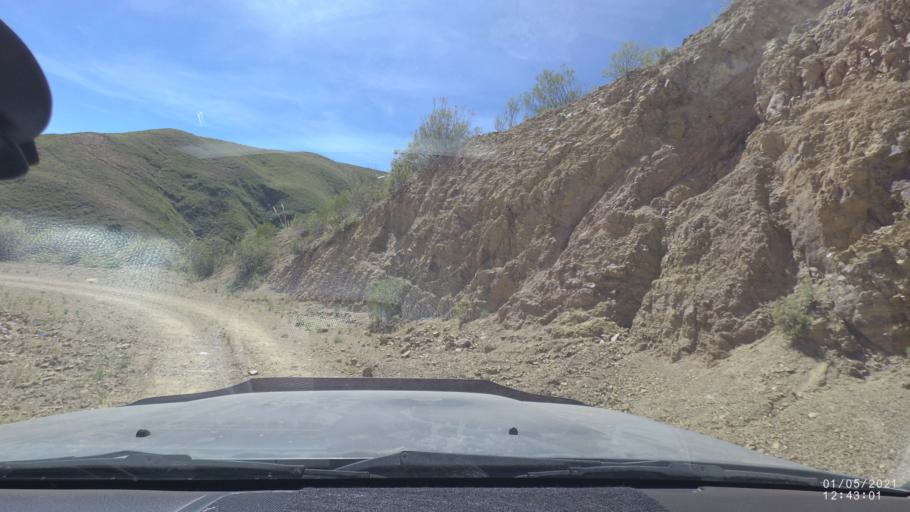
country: BO
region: Cochabamba
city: Capinota
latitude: -17.6794
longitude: -66.1598
